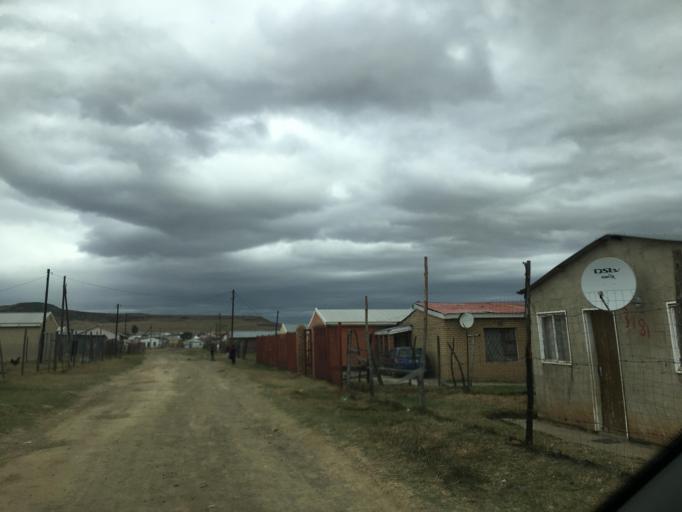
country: ZA
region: Eastern Cape
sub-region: Chris Hani District Municipality
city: Cala
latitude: -31.5330
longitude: 27.6999
